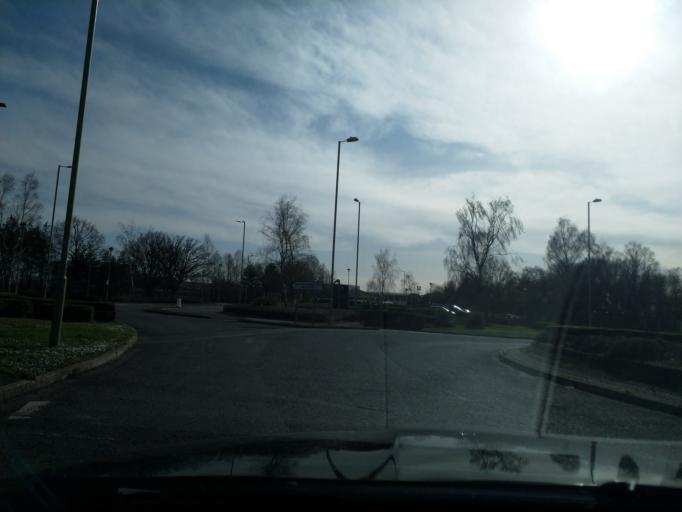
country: GB
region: England
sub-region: Hampshire
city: Farnborough
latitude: 51.2818
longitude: -0.7908
